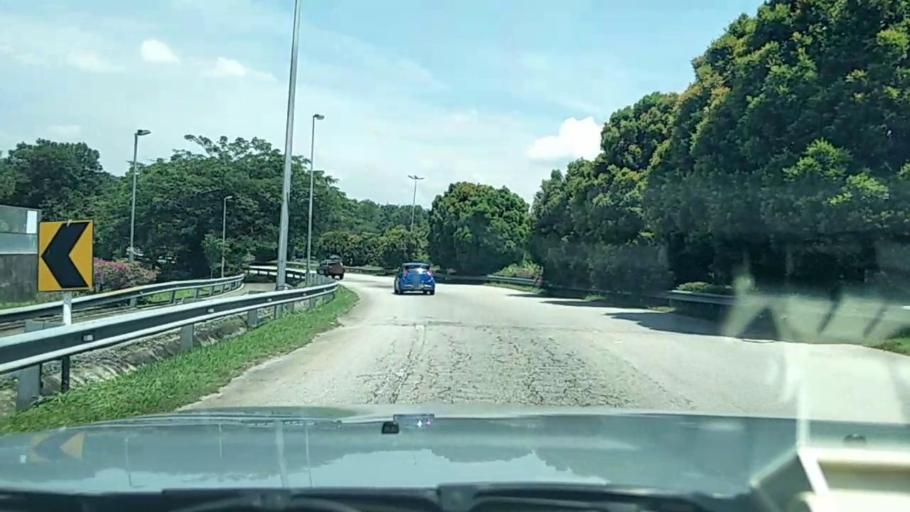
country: MY
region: Putrajaya
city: Putrajaya
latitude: 2.9437
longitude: 101.6661
